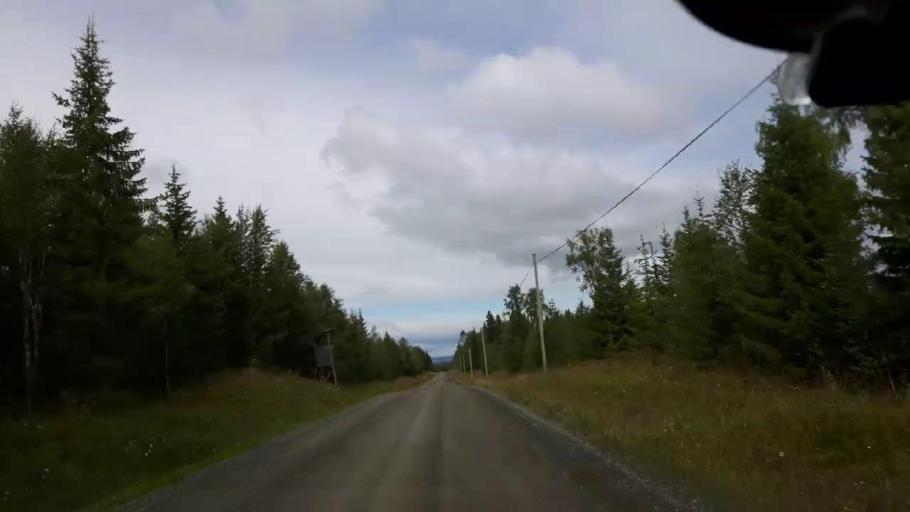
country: SE
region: Jaemtland
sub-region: Krokoms Kommun
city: Krokom
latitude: 63.3834
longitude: 14.1196
